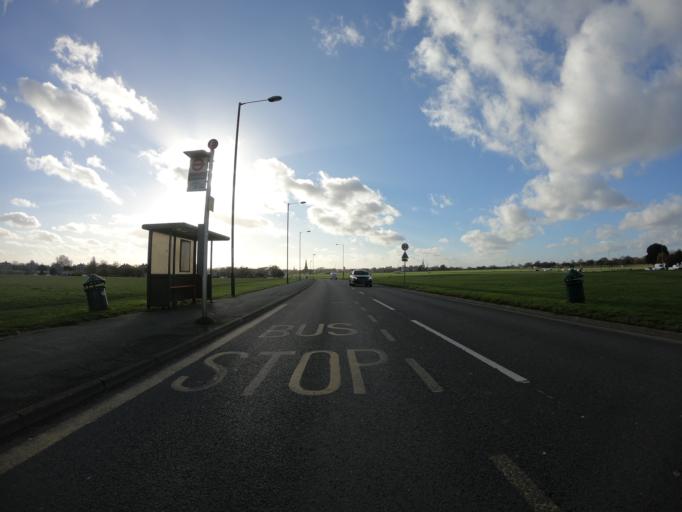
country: GB
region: England
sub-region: Greater London
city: Blackheath
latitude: 51.4729
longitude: 0.0148
